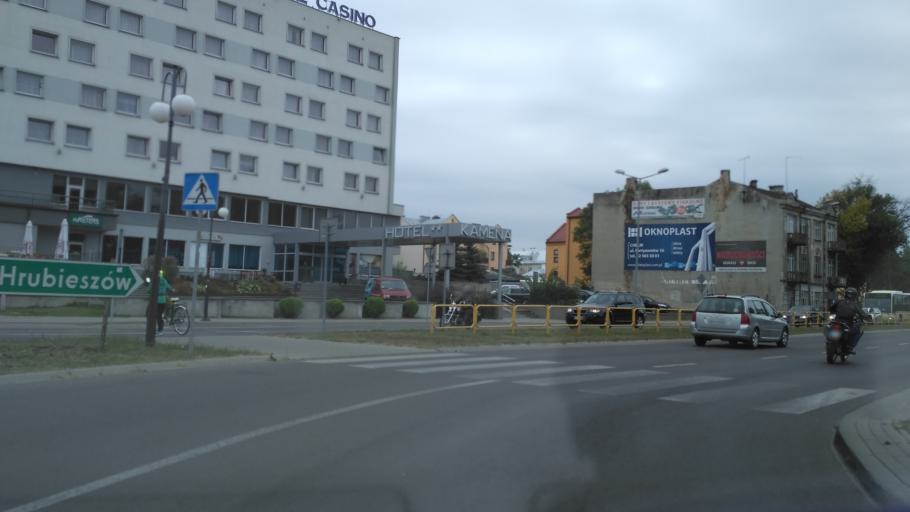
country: PL
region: Lublin Voivodeship
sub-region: Chelm
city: Chelm
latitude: 51.1361
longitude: 23.4668
